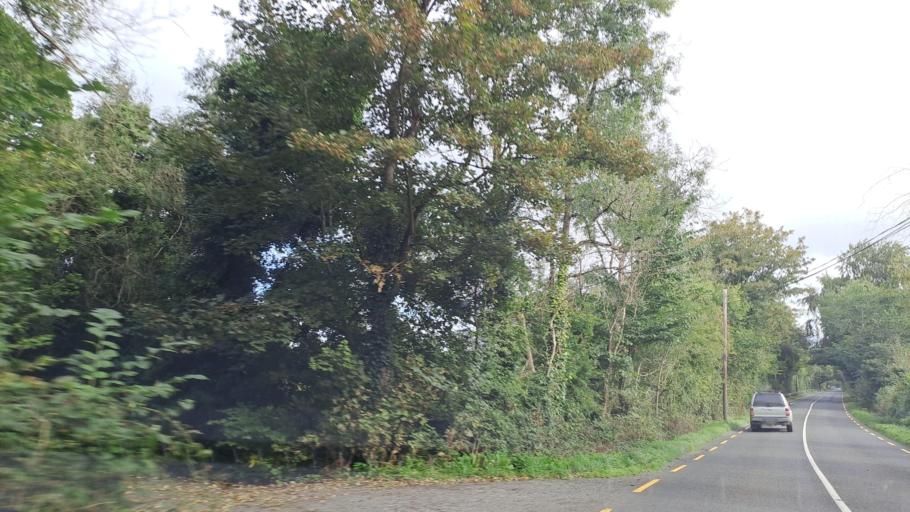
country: IE
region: Ulster
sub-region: County Monaghan
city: Carrickmacross
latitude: 53.9617
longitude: -6.7493
